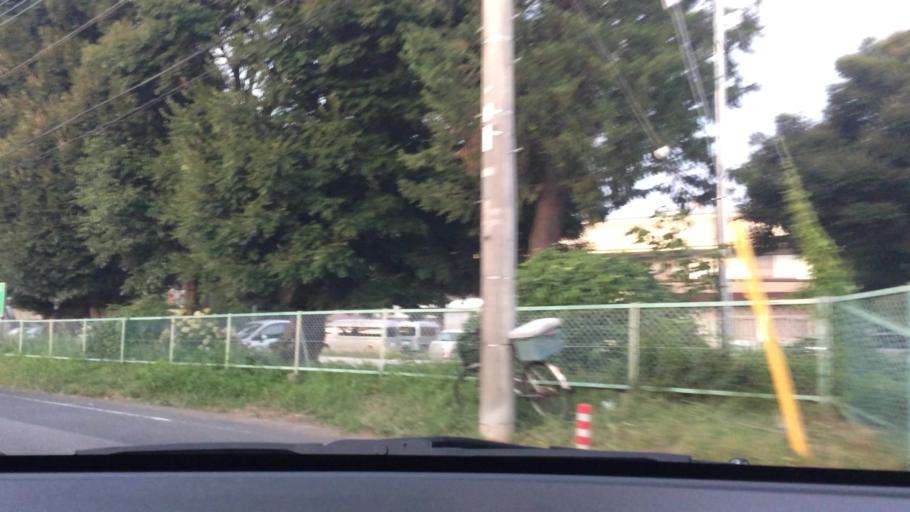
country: JP
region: Chiba
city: Kashiwa
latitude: 35.8880
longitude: 139.9396
